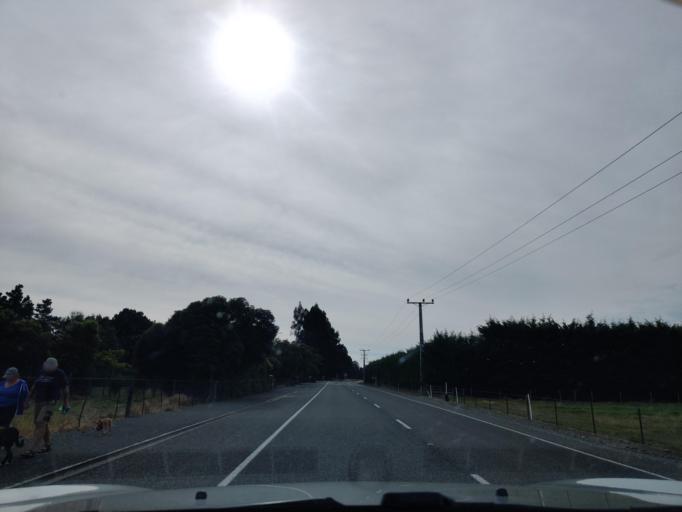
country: NZ
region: Nelson
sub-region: Nelson City
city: Nelson
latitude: -41.5610
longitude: 173.5414
